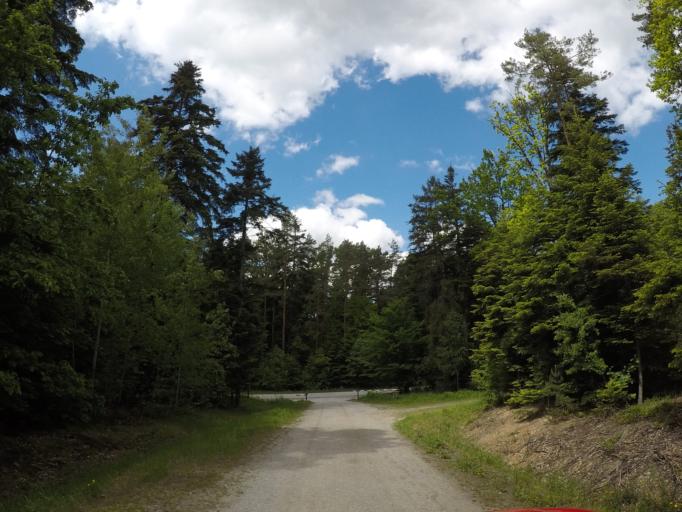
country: PL
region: Swietokrzyskie
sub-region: Powiat kielecki
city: Kostomloty Pierwsze
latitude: 50.9173
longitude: 20.6423
